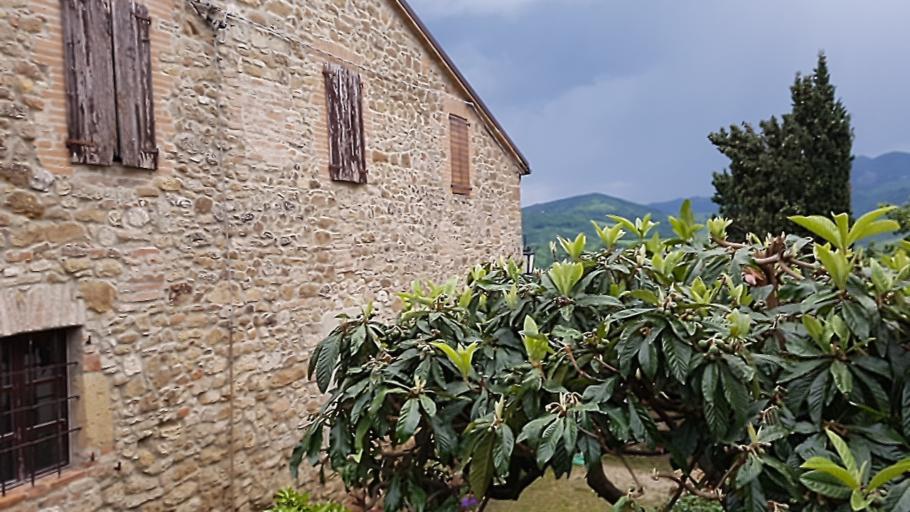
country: IT
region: Emilia-Romagna
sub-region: Provincia di Piacenza
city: Castell'Arquato
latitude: 44.8170
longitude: 9.9017
